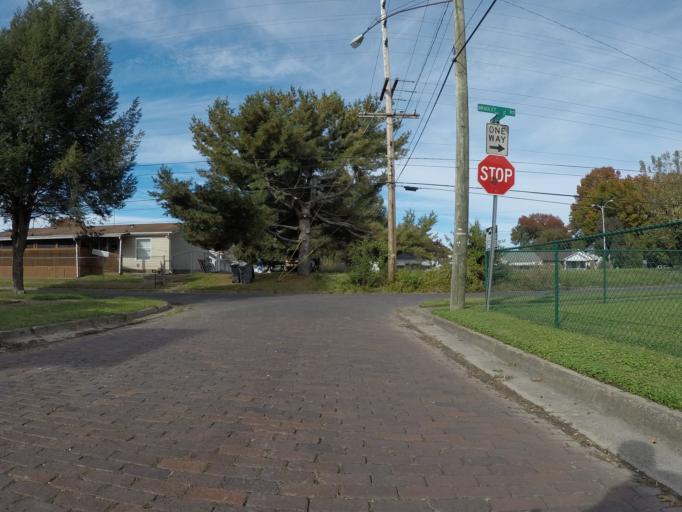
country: US
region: Ohio
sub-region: Lawrence County
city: Burlington
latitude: 38.4027
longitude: -82.5036
